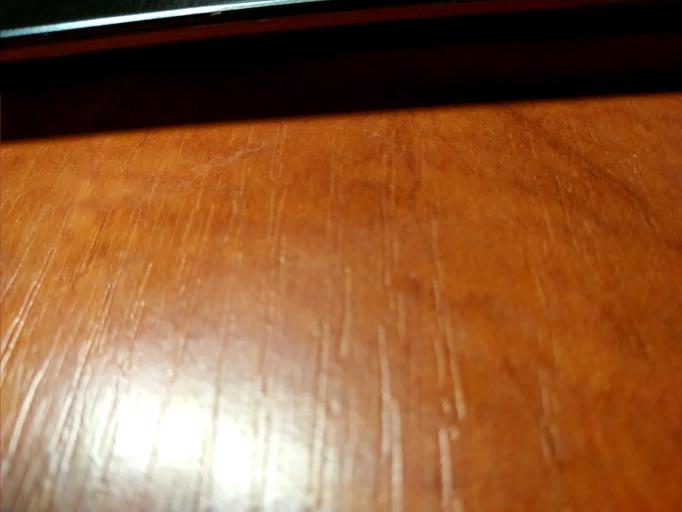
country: RU
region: Arkhangelskaya
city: Onega
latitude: 63.5975
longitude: 36.8662
